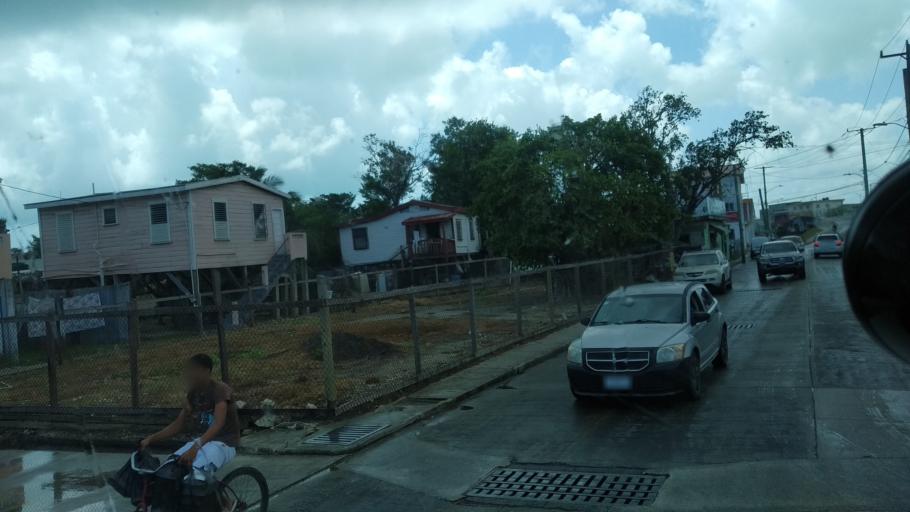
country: BZ
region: Belize
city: Belize City
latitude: 17.5005
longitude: -88.1911
